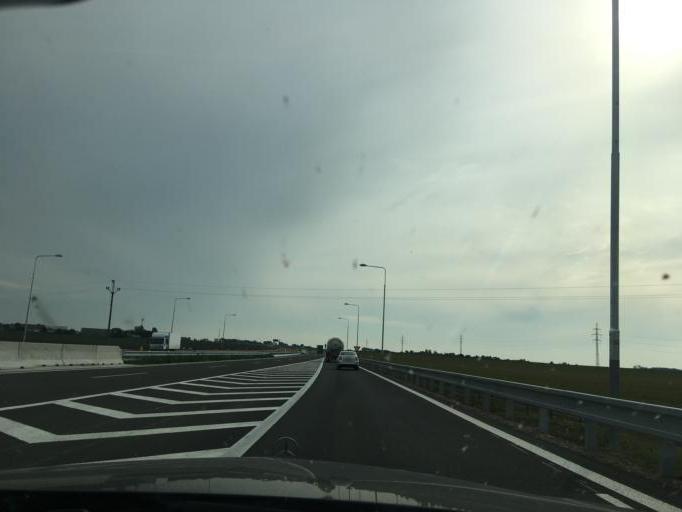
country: CZ
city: Stezery
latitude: 50.1977
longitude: 15.7647
